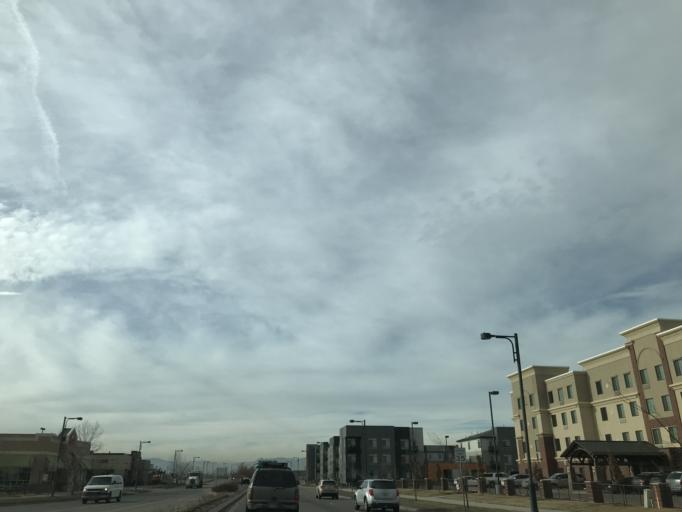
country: US
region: Colorado
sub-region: Adams County
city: Commerce City
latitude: 39.7856
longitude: -104.8935
